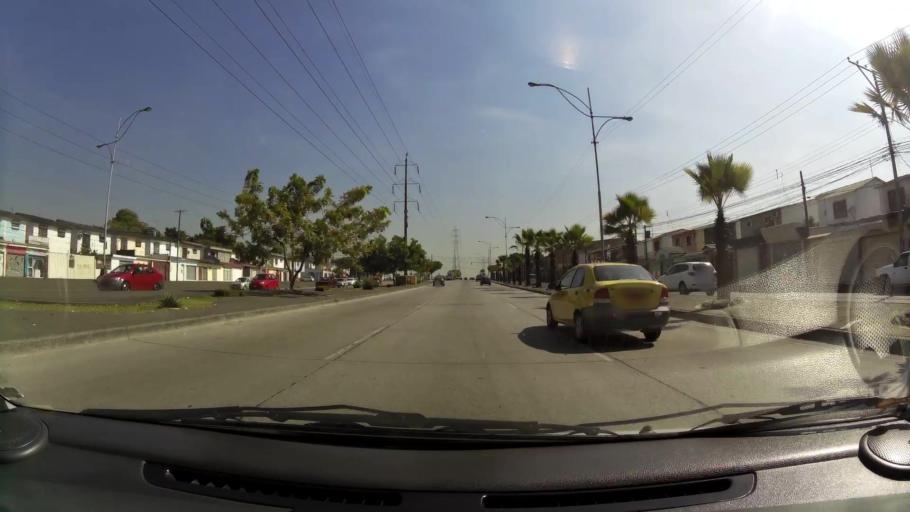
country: EC
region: Guayas
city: Eloy Alfaro
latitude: -2.1110
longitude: -79.9079
